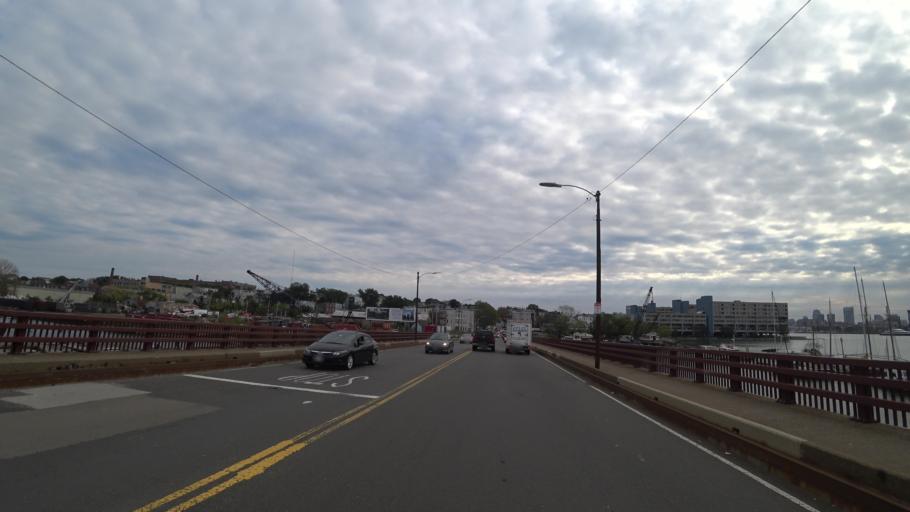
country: US
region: Massachusetts
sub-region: Suffolk County
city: Chelsea
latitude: 42.3847
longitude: -71.0394
